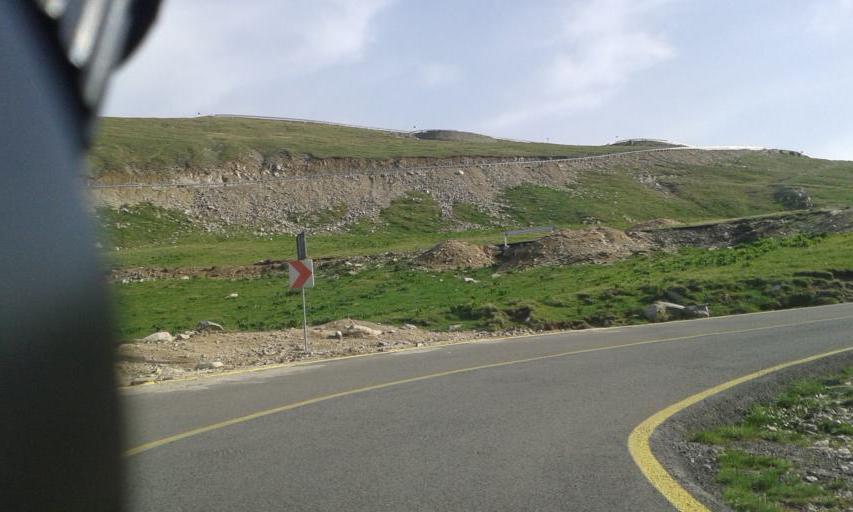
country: RO
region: Gorj
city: Novaci-Straini
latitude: 45.3516
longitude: 23.6537
